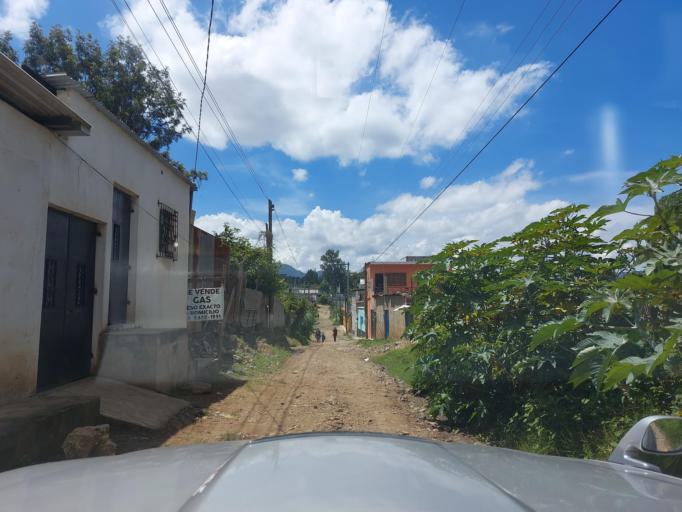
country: GT
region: Chimaltenango
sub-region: Municipio de Chimaltenango
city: Chimaltenango
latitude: 14.6448
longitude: -90.8140
